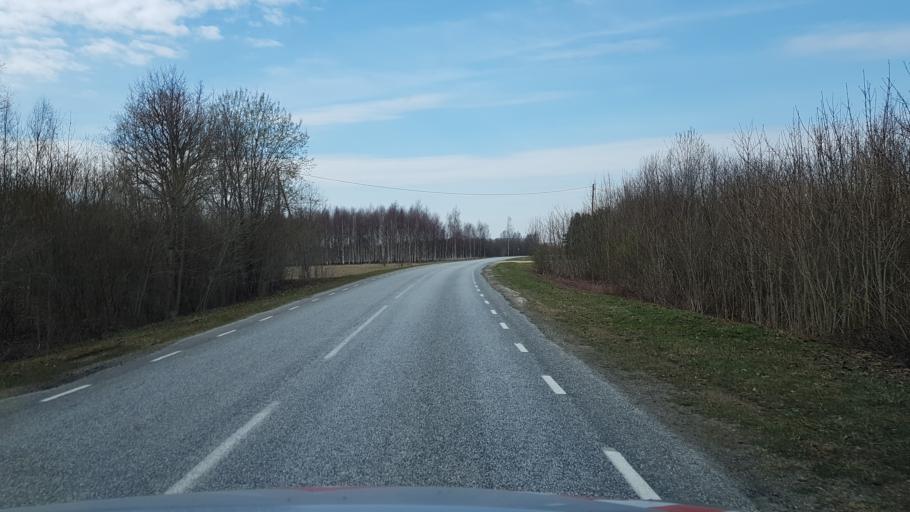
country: EE
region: Laeaene-Virumaa
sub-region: Haljala vald
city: Haljala
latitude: 59.4773
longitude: 26.1589
